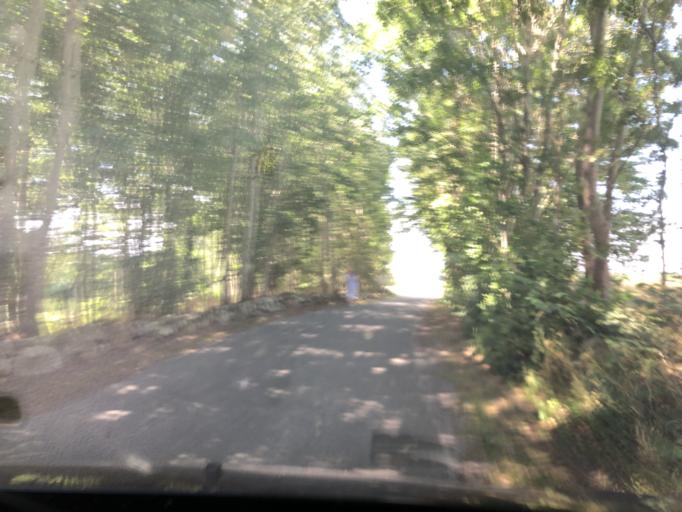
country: DK
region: South Denmark
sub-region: AEro Kommune
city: AEroskobing
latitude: 54.9200
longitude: 10.2819
